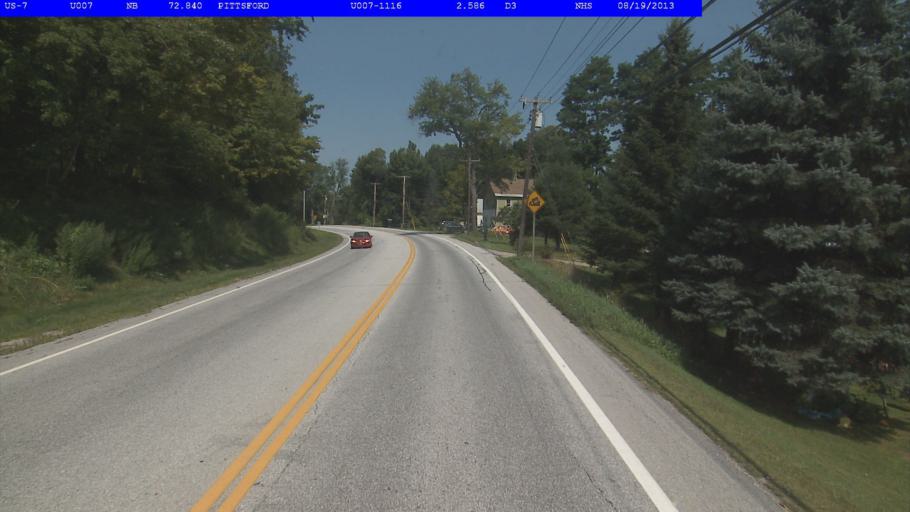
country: US
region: Vermont
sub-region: Rutland County
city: Rutland
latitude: 43.6984
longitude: -73.0063
